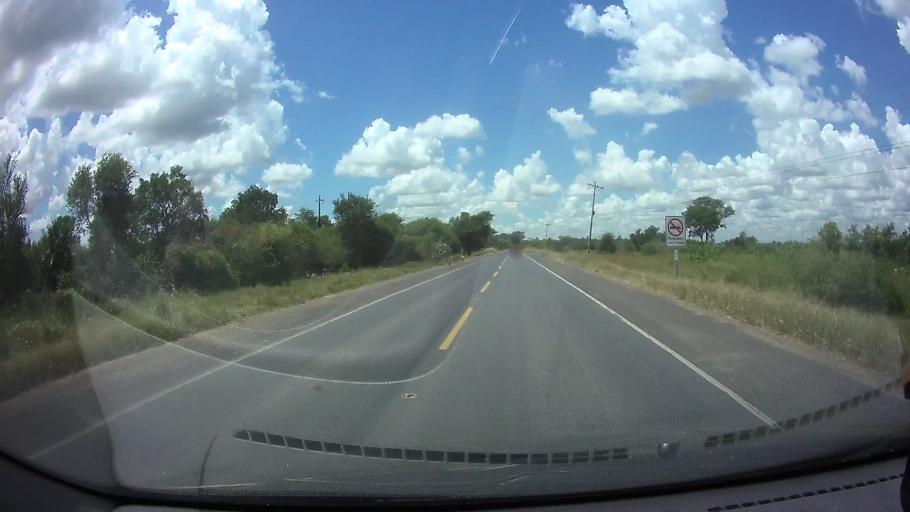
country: PY
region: Presidente Hayes
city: Nanawa
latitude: -25.1934
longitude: -57.6296
